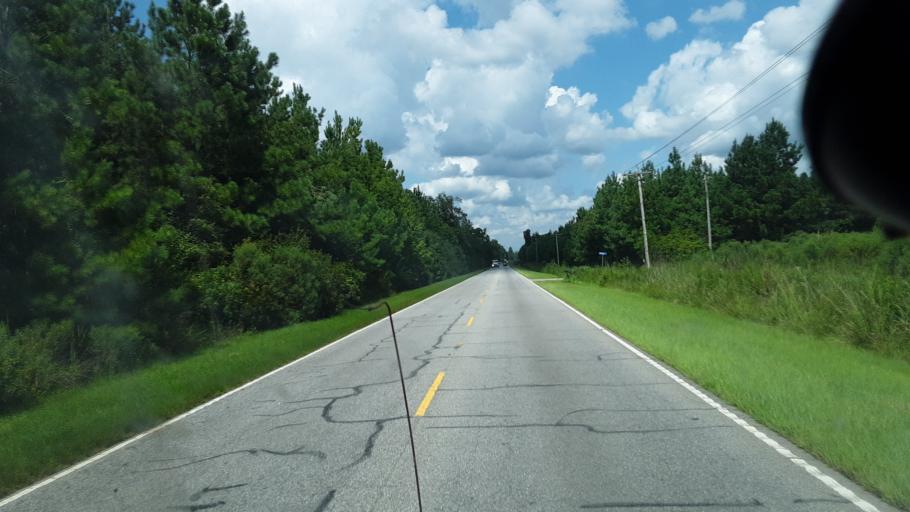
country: US
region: South Carolina
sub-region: Williamsburg County
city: Andrews
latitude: 33.6102
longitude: -79.4376
